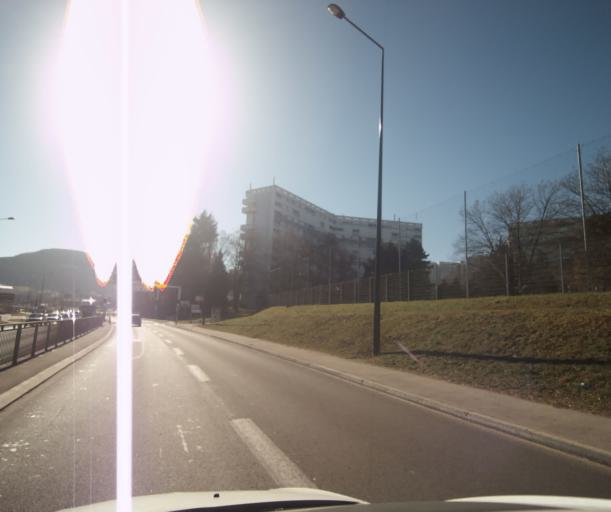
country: FR
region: Franche-Comte
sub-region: Departement du Doubs
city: Avanne-Aveney
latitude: 47.2242
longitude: 5.9789
